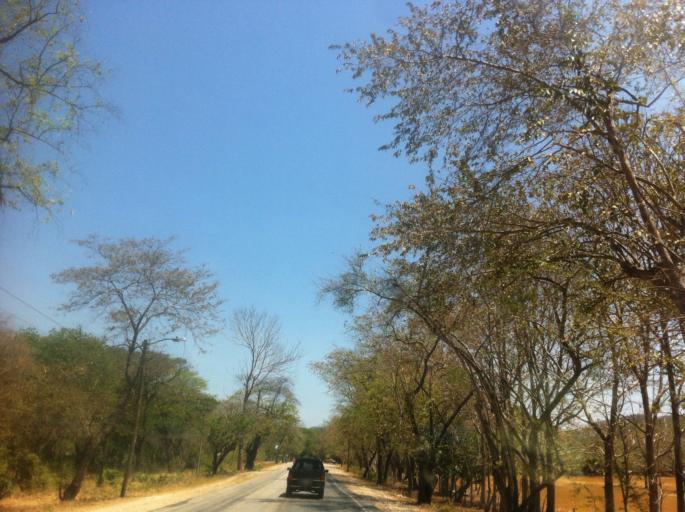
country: CR
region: Guanacaste
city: Santa Cruz
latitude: 10.2805
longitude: -85.5908
